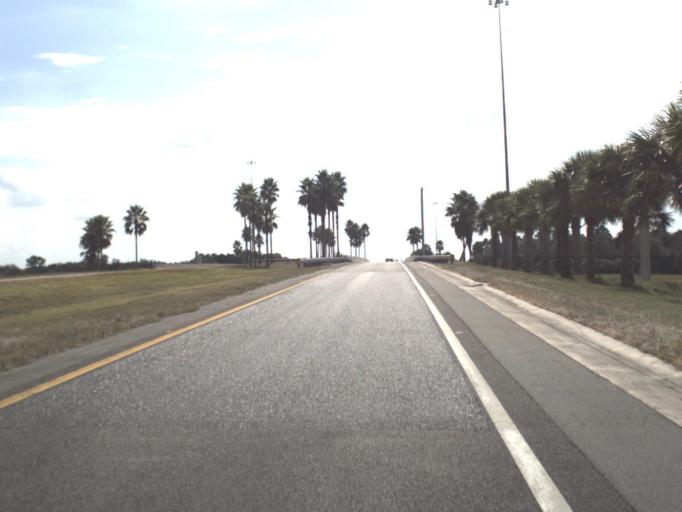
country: US
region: Florida
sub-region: Polk County
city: Polk City
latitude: 28.1560
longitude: -81.8473
